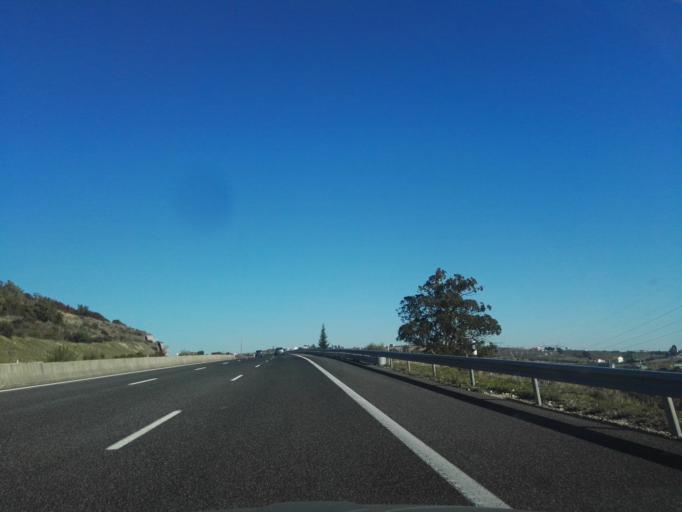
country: PT
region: Lisbon
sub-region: Arruda Dos Vinhos
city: Arruda dos Vinhos
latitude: 38.9528
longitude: -9.0645
